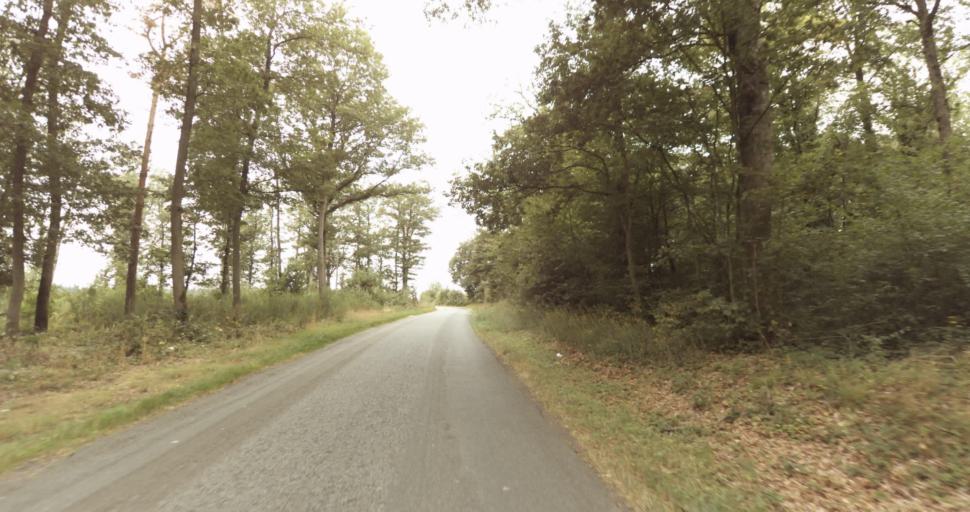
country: FR
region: Haute-Normandie
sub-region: Departement de l'Eure
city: Saint-Germain-sur-Avre
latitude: 48.8307
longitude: 1.2552
